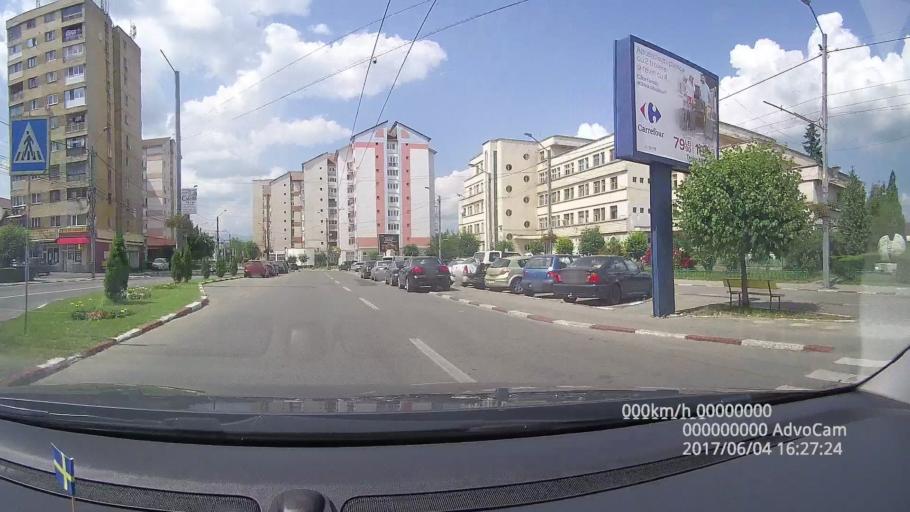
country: RO
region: Gorj
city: Targu Jiu
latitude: 45.0326
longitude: 23.2790
